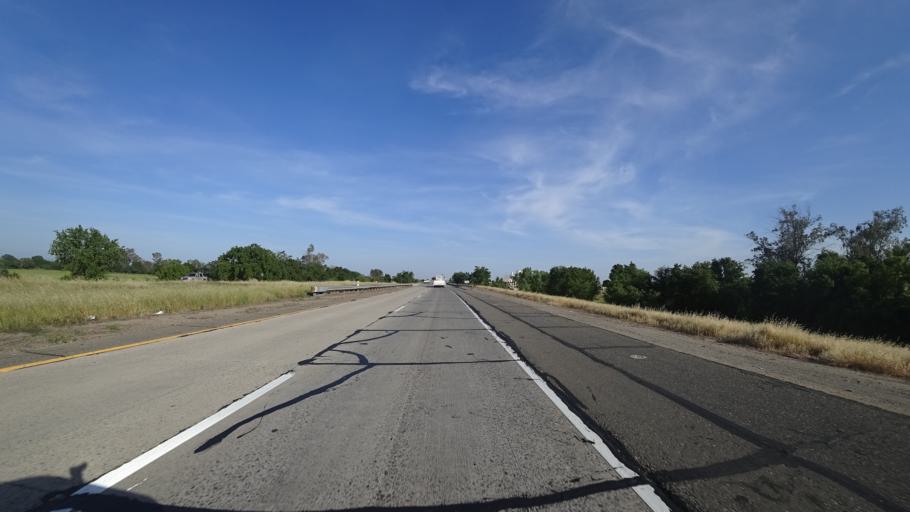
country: US
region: California
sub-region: Yuba County
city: Olivehurst
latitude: 39.0718
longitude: -121.5232
